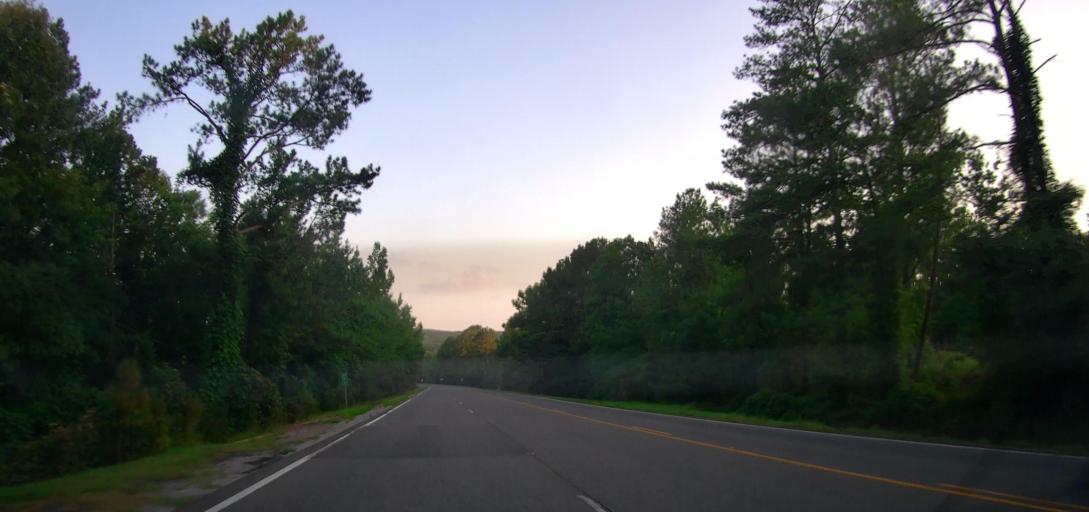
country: US
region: Alabama
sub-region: Marion County
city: Hamilton
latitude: 34.0777
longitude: -87.9767
